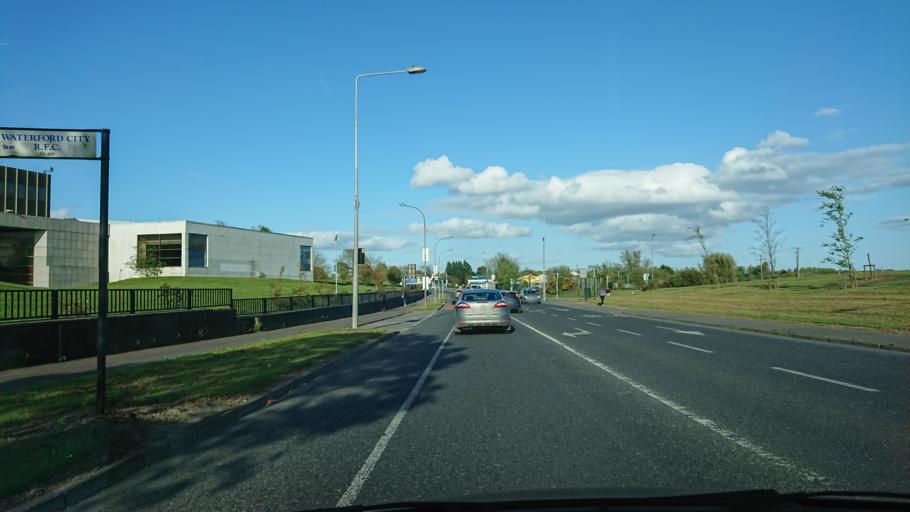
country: IE
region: Munster
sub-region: Waterford
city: Waterford
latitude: 52.2451
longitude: -7.1333
